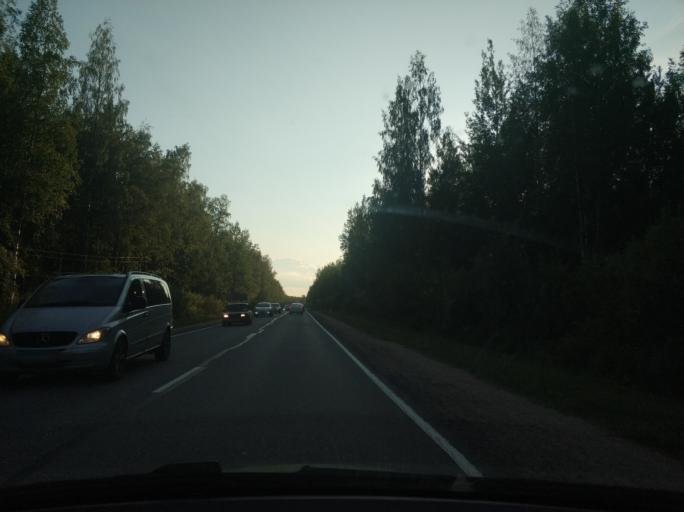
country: RU
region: Leningrad
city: Borisova Griva
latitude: 60.0818
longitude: 31.0478
